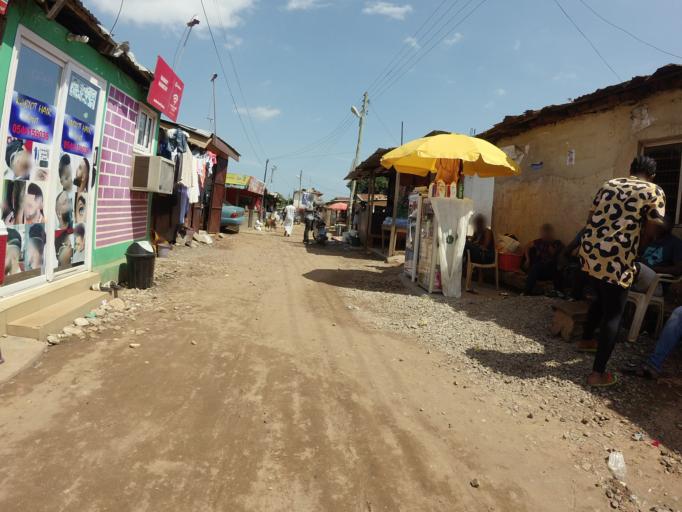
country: GH
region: Greater Accra
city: Accra
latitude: 5.5815
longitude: -0.1968
